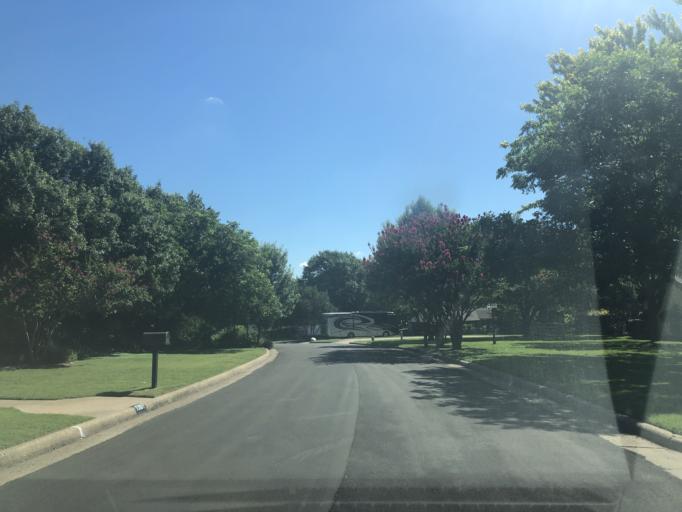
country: US
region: Texas
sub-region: Dallas County
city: Duncanville
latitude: 32.6355
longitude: -96.9381
